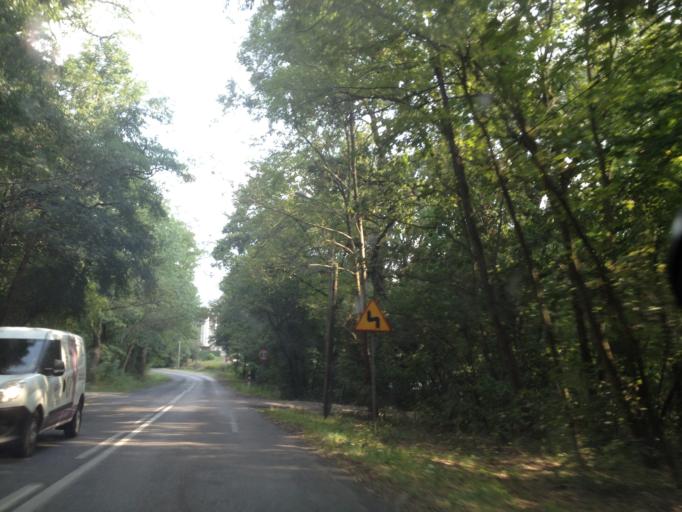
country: PL
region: Greater Poland Voivodeship
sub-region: Powiat poznanski
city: Rogalinek
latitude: 52.2333
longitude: 16.9357
